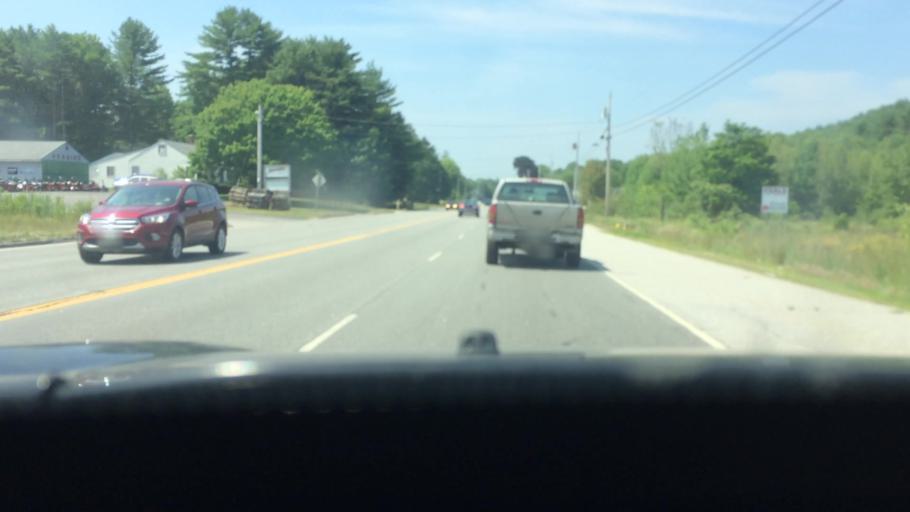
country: US
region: Maine
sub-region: Androscoggin County
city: Minot
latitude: 44.0800
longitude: -70.2859
